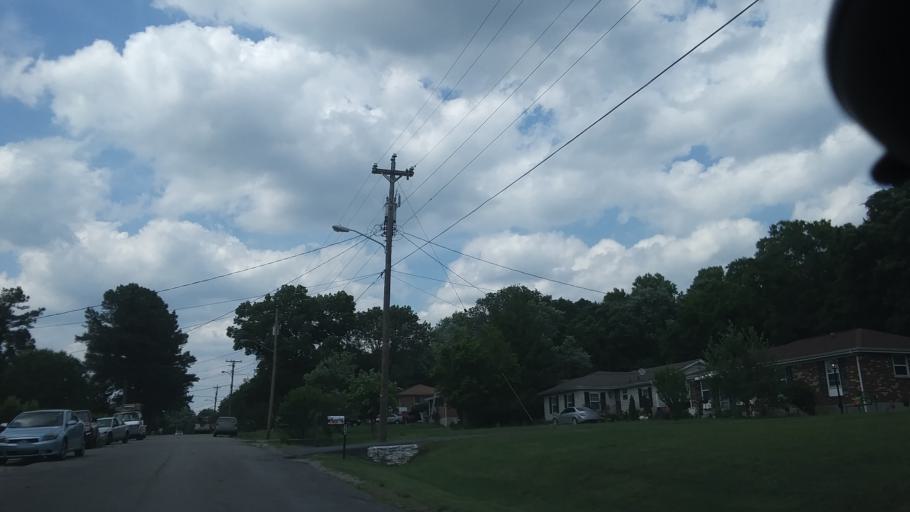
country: US
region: Tennessee
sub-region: Rutherford County
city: La Vergne
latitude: 36.0969
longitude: -86.6645
